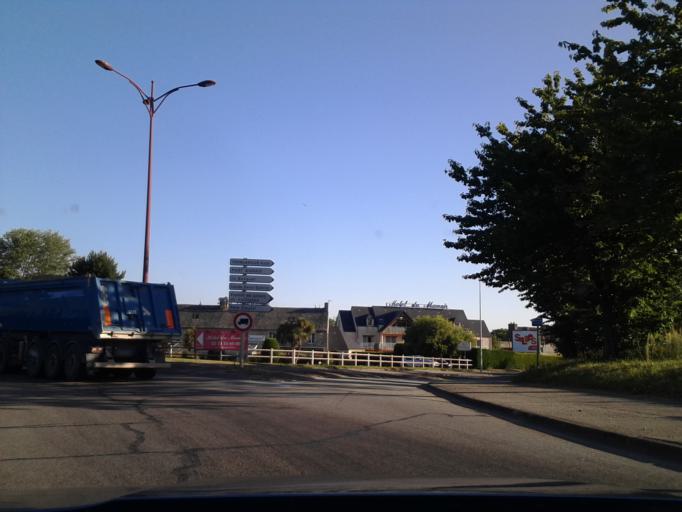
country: FR
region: Lower Normandy
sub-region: Departement de la Manche
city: Tourlaville
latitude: 49.6359
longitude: -1.5756
